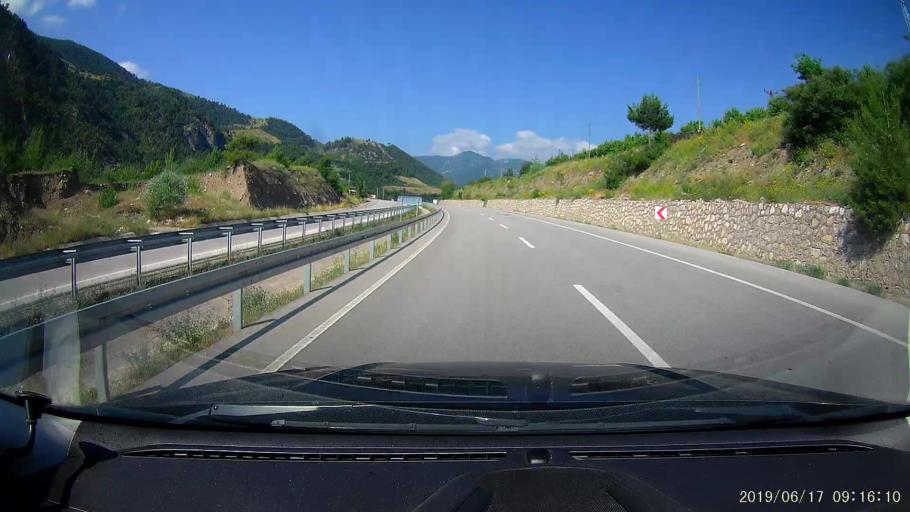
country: TR
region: Amasya
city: Akdag
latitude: 40.7459
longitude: 36.0184
